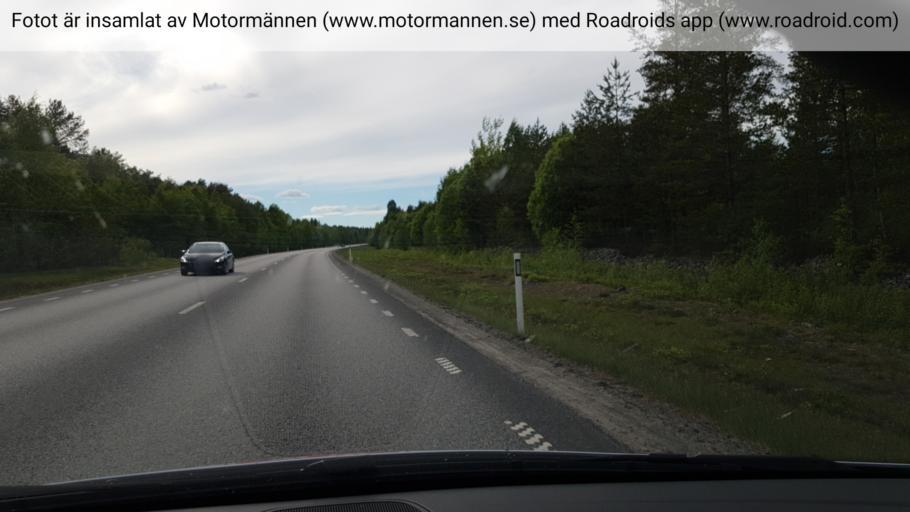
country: SE
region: Vaesterbotten
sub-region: Umea Kommun
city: Roback
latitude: 63.8476
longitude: 20.1374
